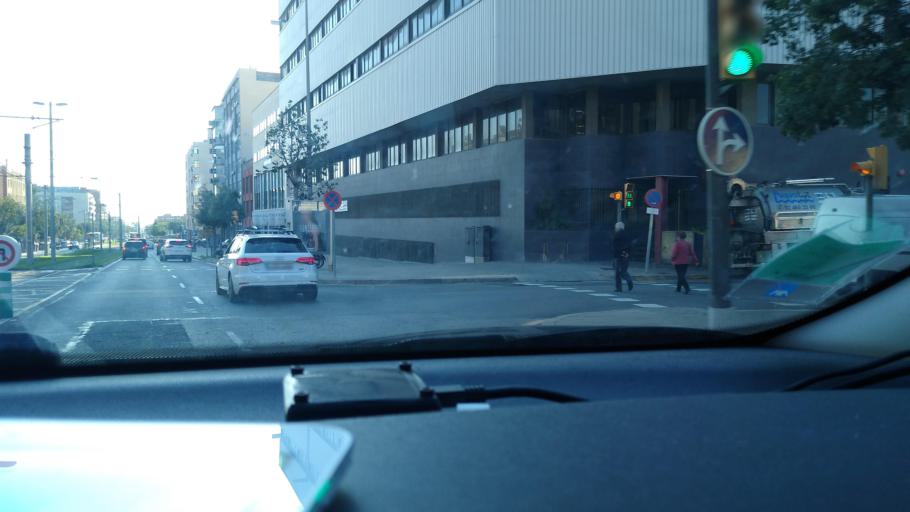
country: ES
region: Catalonia
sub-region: Provincia de Barcelona
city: Esplugues de Llobregat
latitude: 41.3710
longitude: 2.0823
